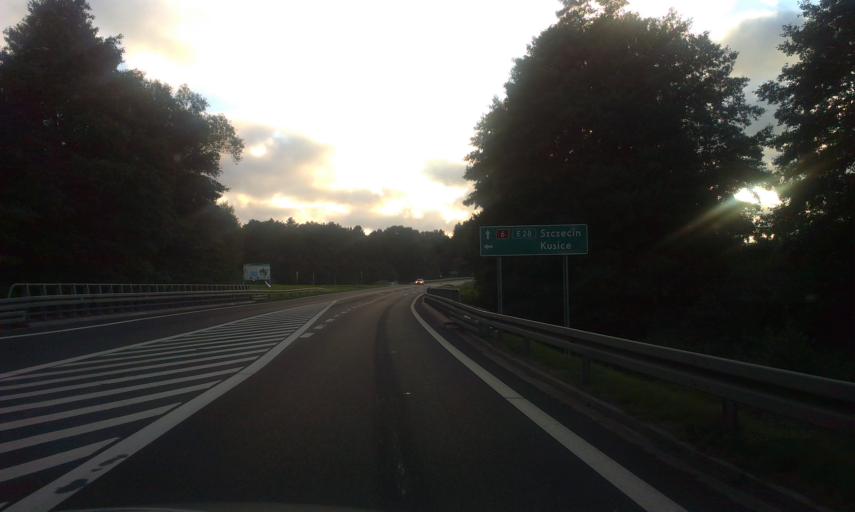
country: PL
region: West Pomeranian Voivodeship
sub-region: Powiat slawienski
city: Darlowo
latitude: 54.2774
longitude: 16.4780
